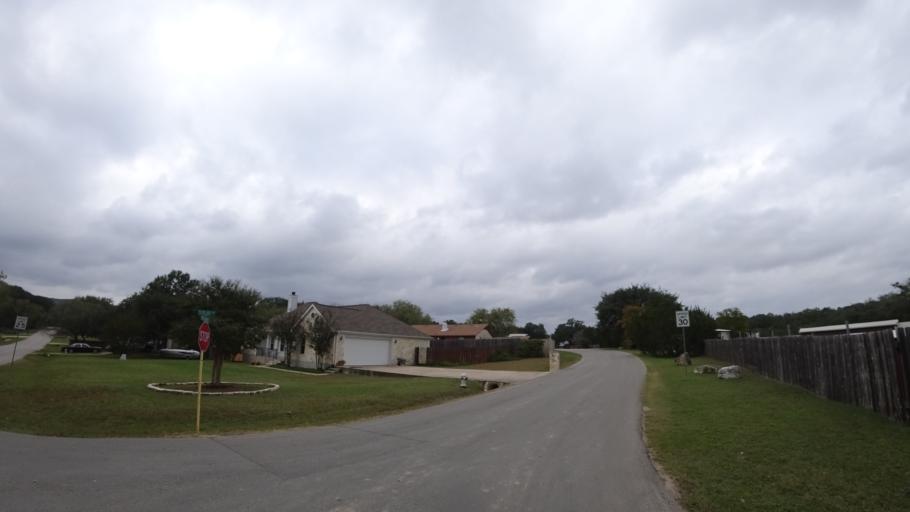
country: US
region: Texas
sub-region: Travis County
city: Bee Cave
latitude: 30.3288
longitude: -97.9198
